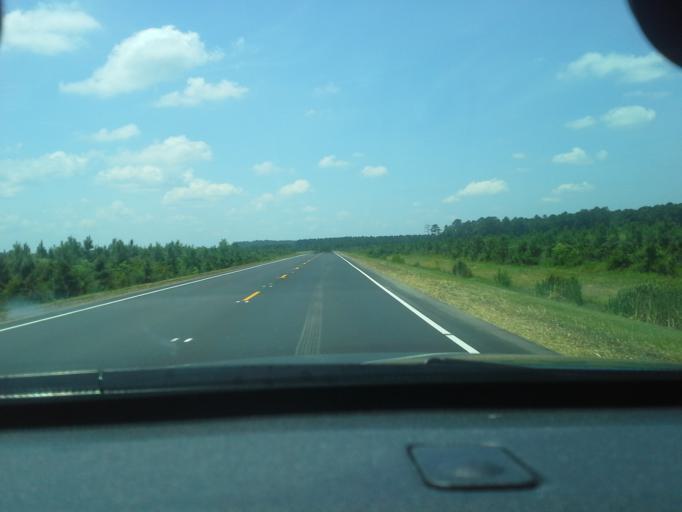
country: US
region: North Carolina
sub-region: Chowan County
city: Edenton
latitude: 35.9263
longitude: -76.5167
